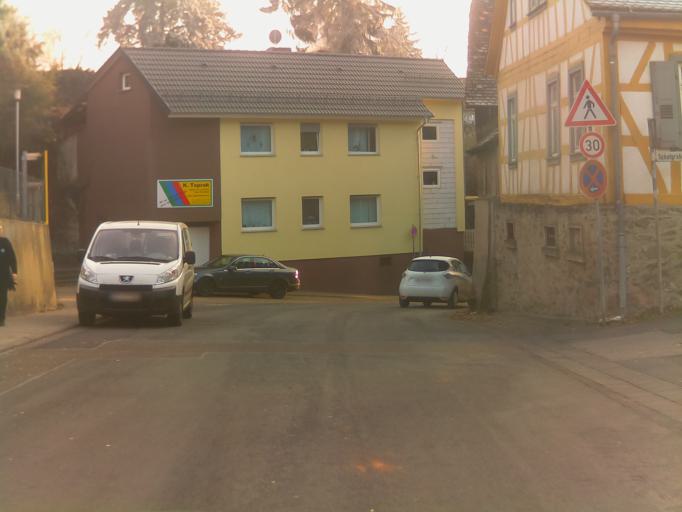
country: DE
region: Hesse
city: Ober-Ramstadt
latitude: 49.8271
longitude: 8.7502
